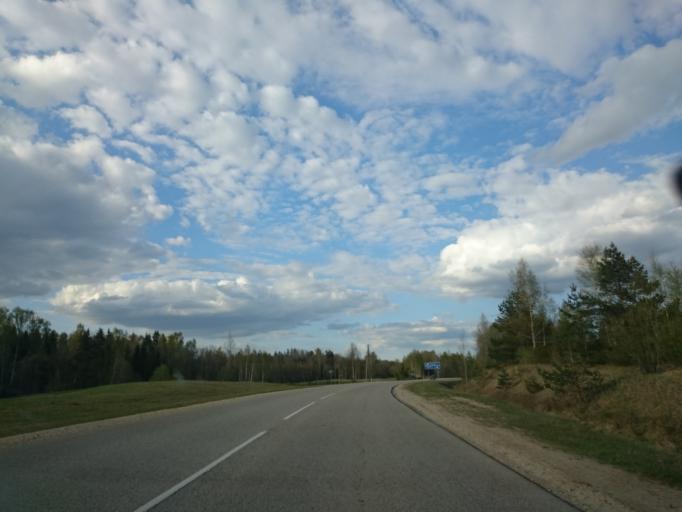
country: LV
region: Kuldigas Rajons
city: Kuldiga
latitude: 56.8703
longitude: 21.8567
